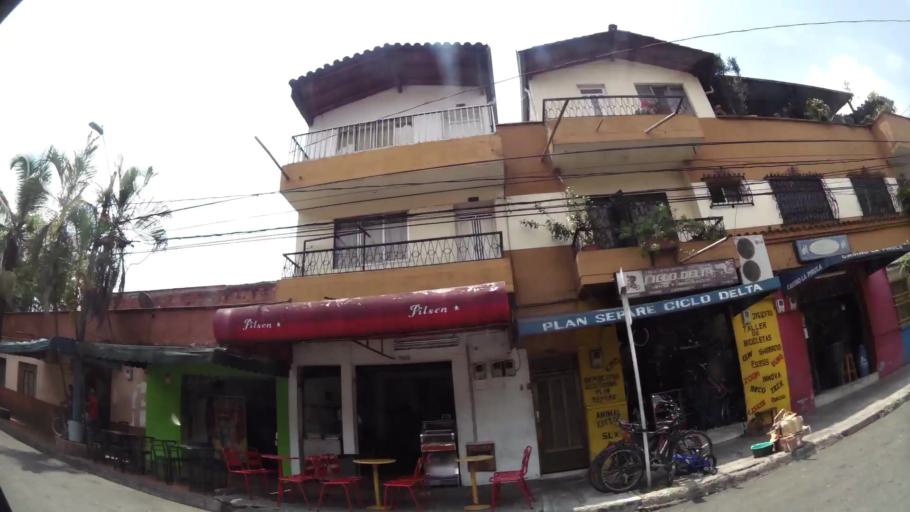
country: CO
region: Antioquia
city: Sabaneta
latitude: 6.1705
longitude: -75.6133
